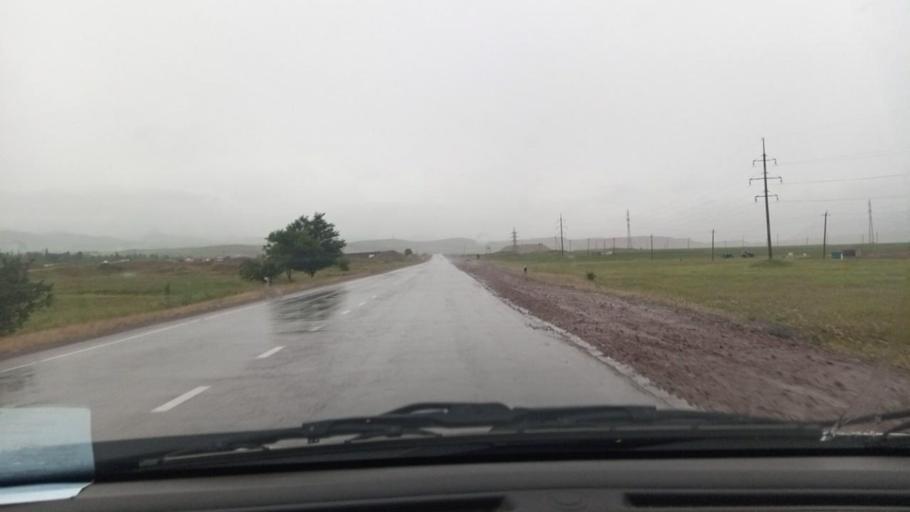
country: UZ
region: Toshkent
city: Angren
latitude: 41.0402
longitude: 70.1508
